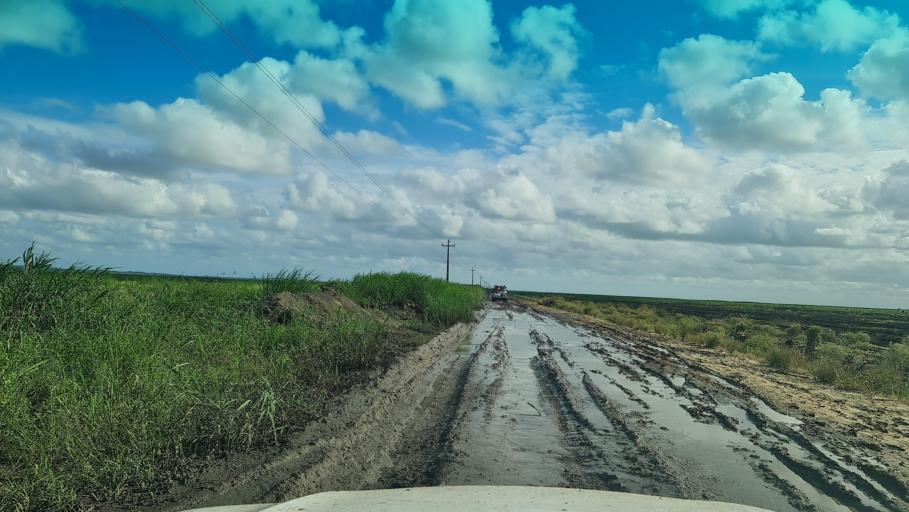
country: MZ
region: Maputo
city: Manhica
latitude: -25.4386
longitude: 32.8406
